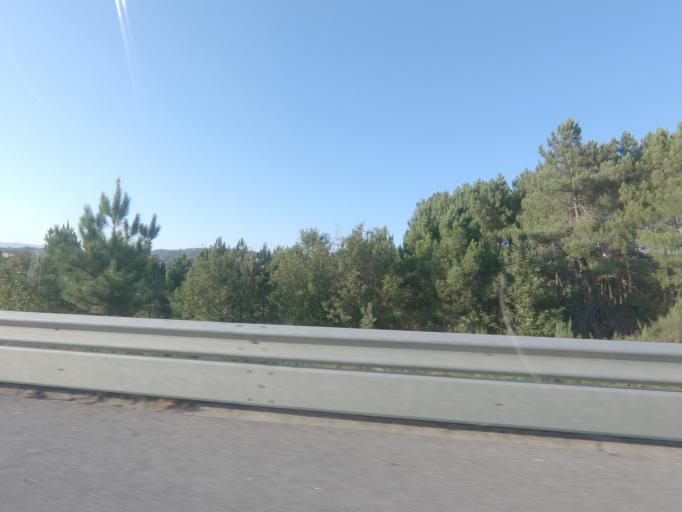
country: PT
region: Vila Real
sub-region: Sabrosa
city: Vilela
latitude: 41.2649
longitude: -7.6305
